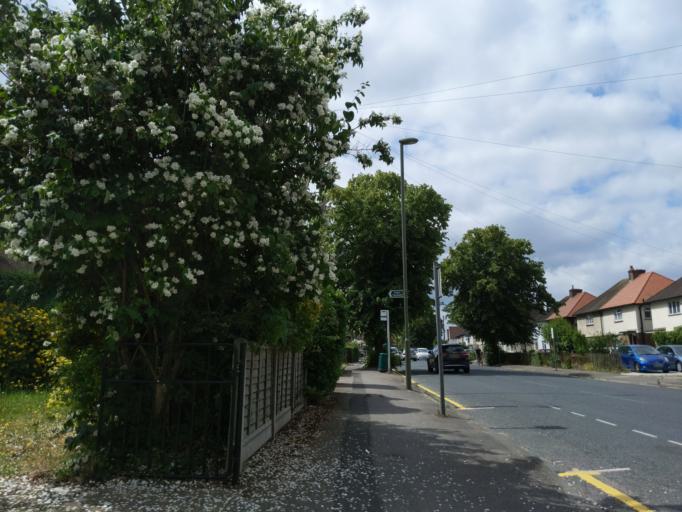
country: GB
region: England
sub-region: Surrey
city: Esher
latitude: 51.3738
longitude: -0.3918
